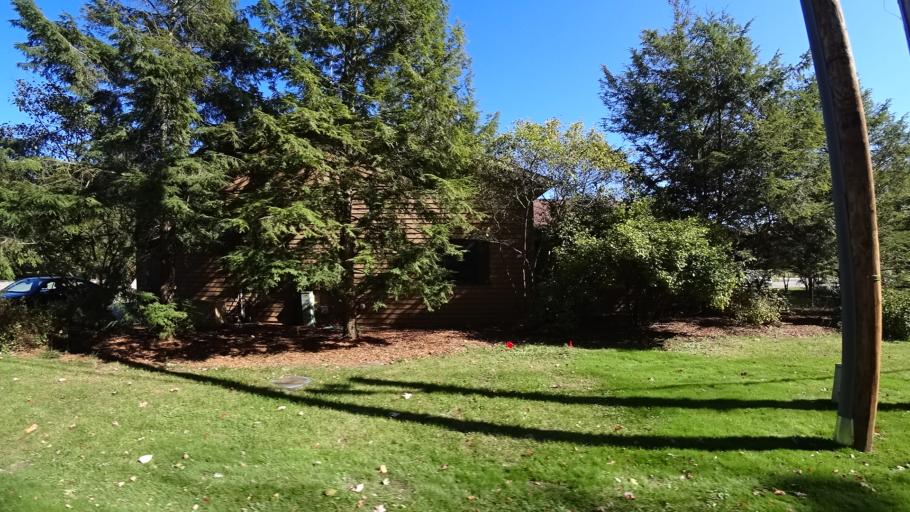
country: US
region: Indiana
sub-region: LaPorte County
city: Long Beach
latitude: 41.7512
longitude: -86.8160
